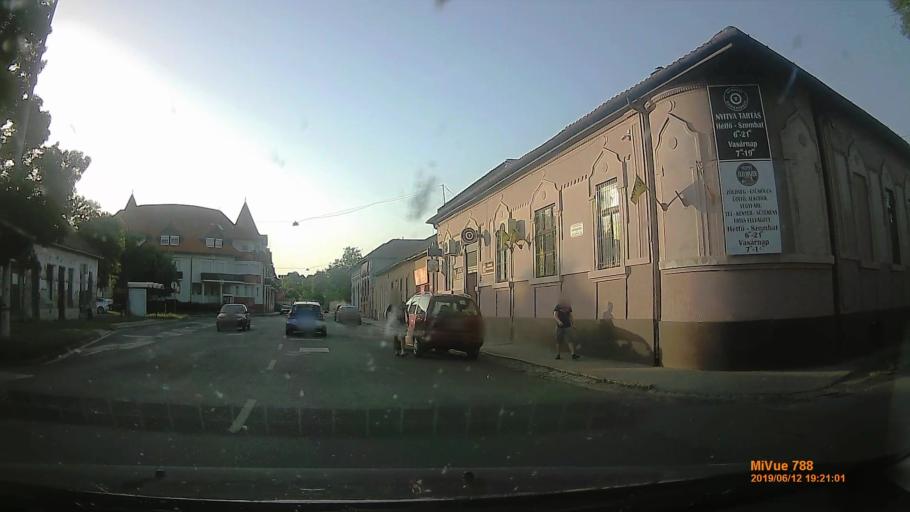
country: HU
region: Bacs-Kiskun
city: Kecskemet
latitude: 46.9033
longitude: 19.7029
